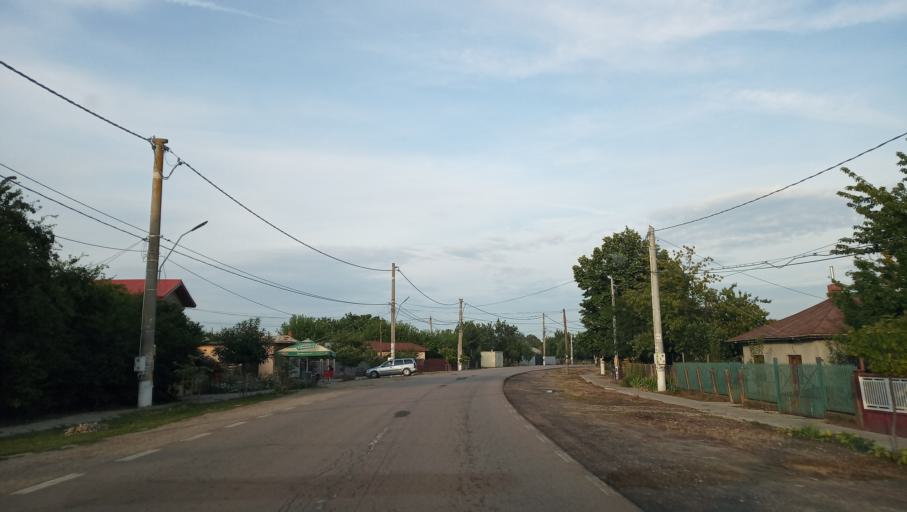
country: RO
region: Giurgiu
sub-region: Comuna Greaca
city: Greaca
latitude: 44.1114
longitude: 26.3301
